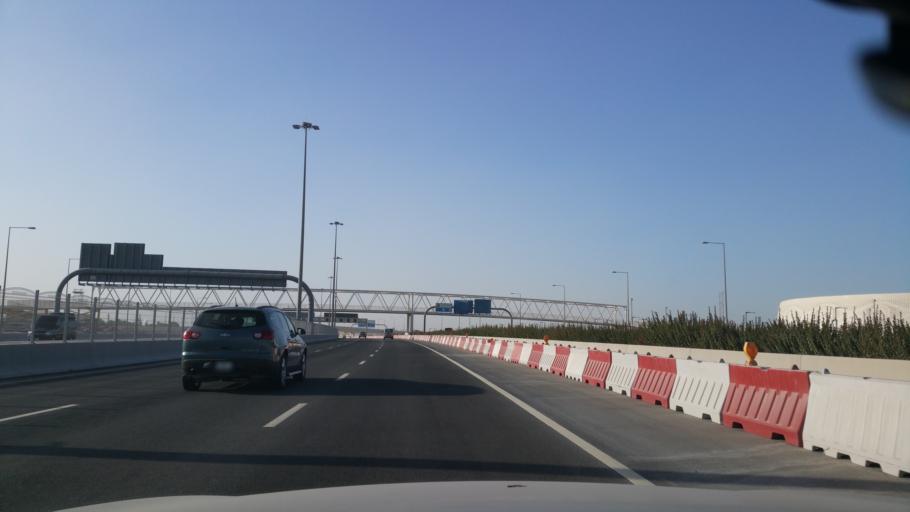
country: QA
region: Baladiyat ad Dawhah
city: Doha
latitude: 25.2295
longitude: 51.5314
